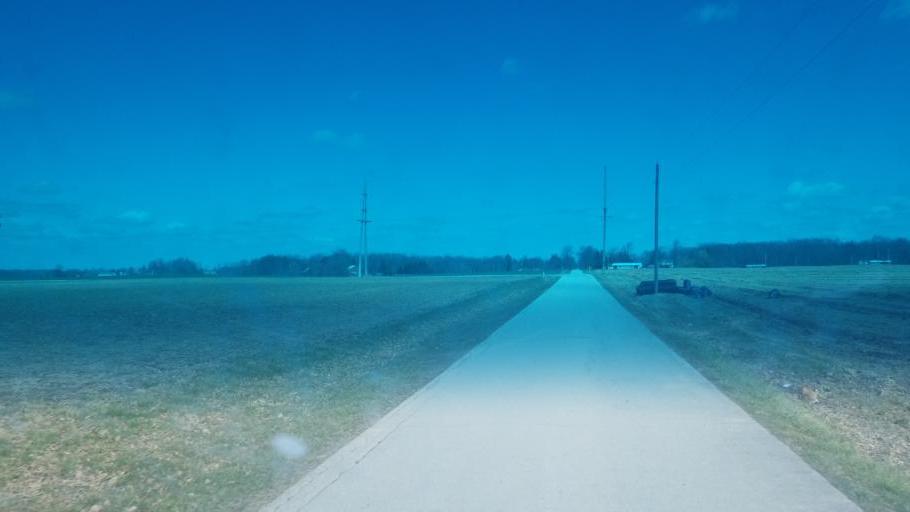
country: US
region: Ohio
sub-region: Crawford County
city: Bucyrus
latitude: 40.8329
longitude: -83.0738
